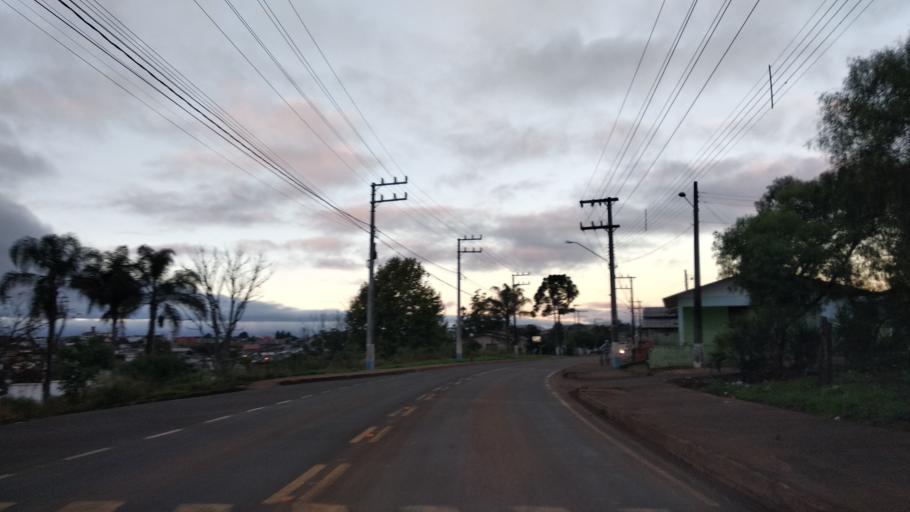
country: BR
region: Santa Catarina
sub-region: Campos Novos
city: Campos Novos
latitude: -27.3827
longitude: -51.2103
